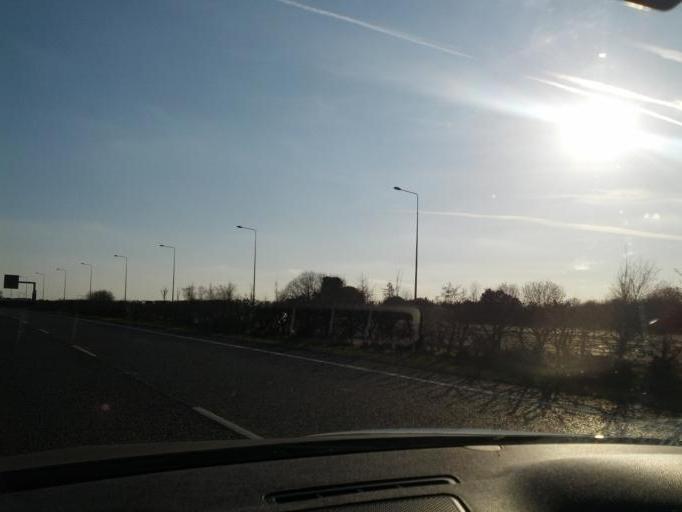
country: IE
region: Leinster
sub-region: Laois
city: Portlaoise
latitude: 53.0476
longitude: -7.2412
